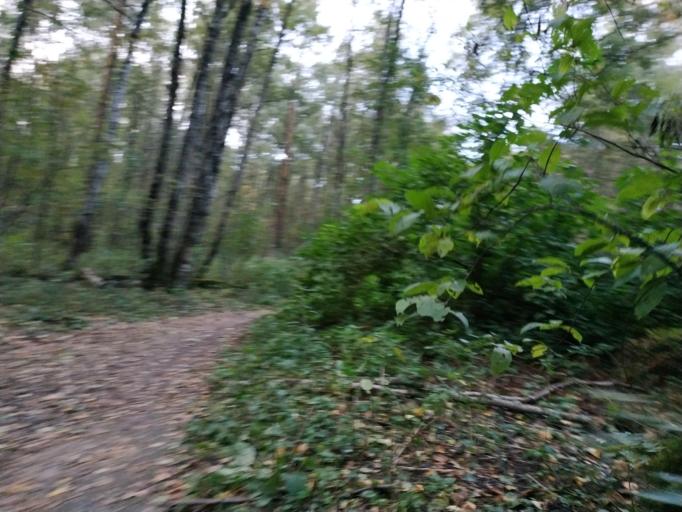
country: RU
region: Moscow
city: Khimki
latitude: 55.8721
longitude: 37.4316
